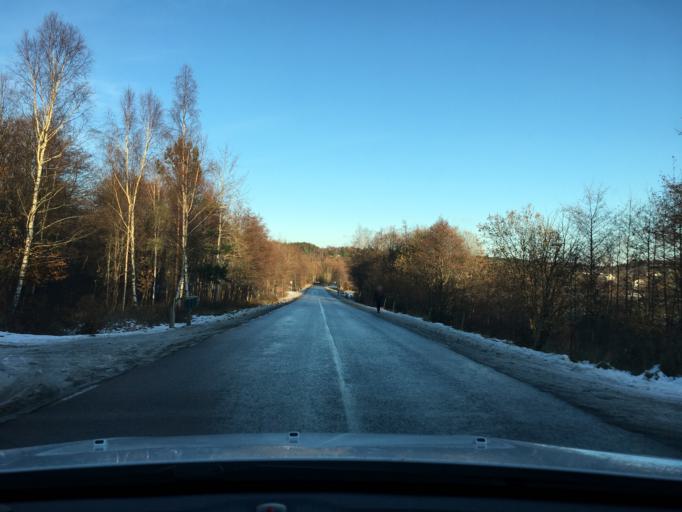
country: SE
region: Vaestra Goetaland
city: Svanesund
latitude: 58.1399
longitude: 11.7823
